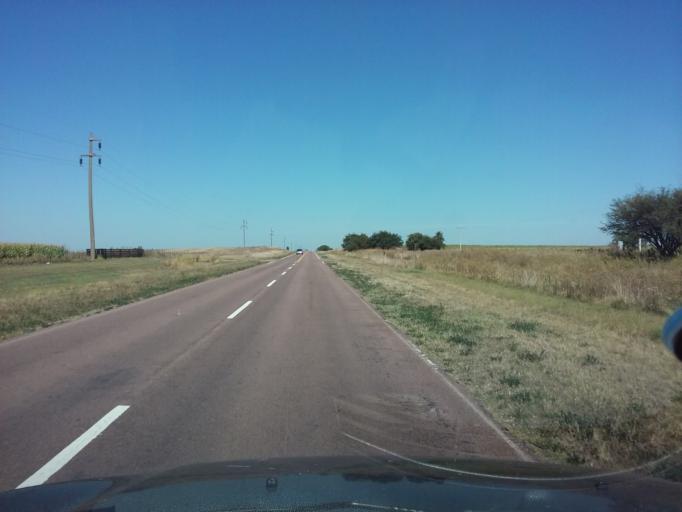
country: AR
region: La Pampa
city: Anguil
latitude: -36.4798
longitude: -63.9436
